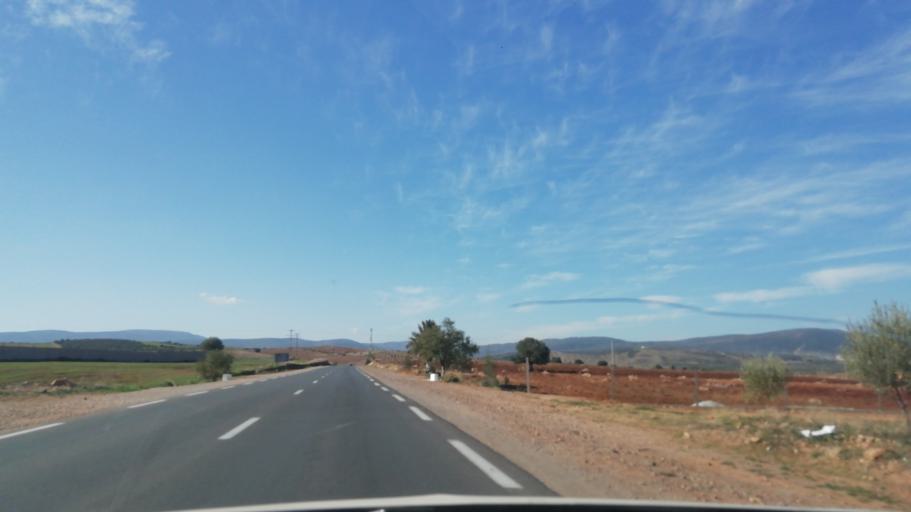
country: DZ
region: Tlemcen
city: Ouled Mimoun
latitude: 34.8776
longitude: -1.1070
